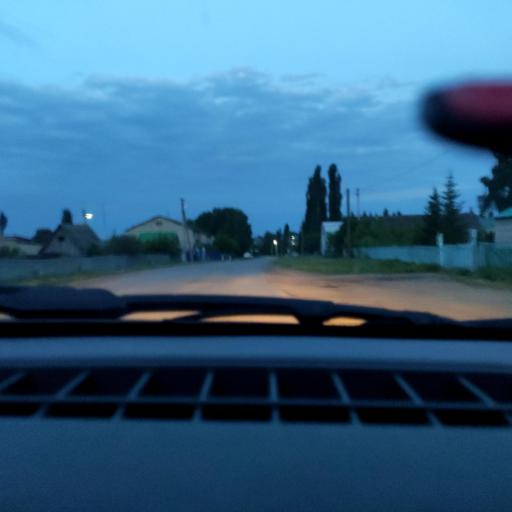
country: RU
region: Bashkortostan
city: Tolbazy
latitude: 54.2927
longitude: 55.8123
